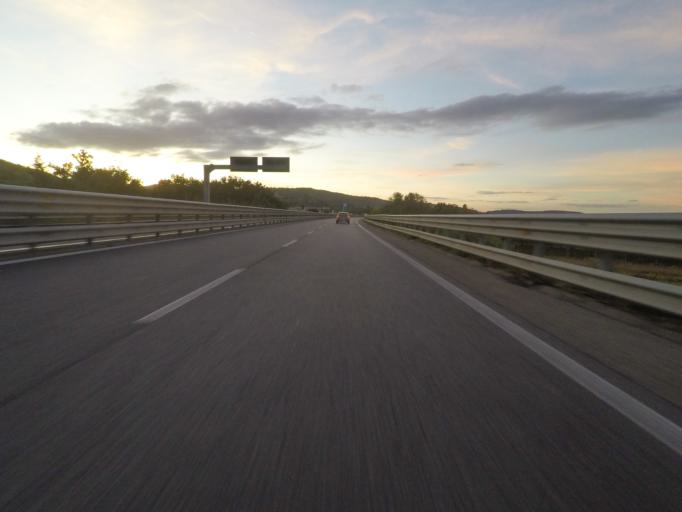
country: IT
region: Tuscany
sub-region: Provincia di Siena
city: Sinalunga
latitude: 43.2264
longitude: 11.7404
